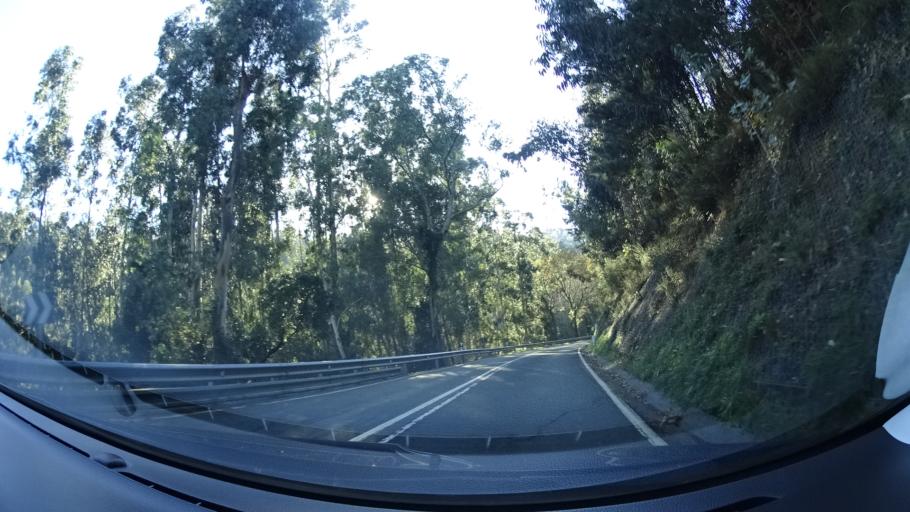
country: ES
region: Basque Country
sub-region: Bizkaia
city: Bermeo
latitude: 43.4328
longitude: -2.7449
